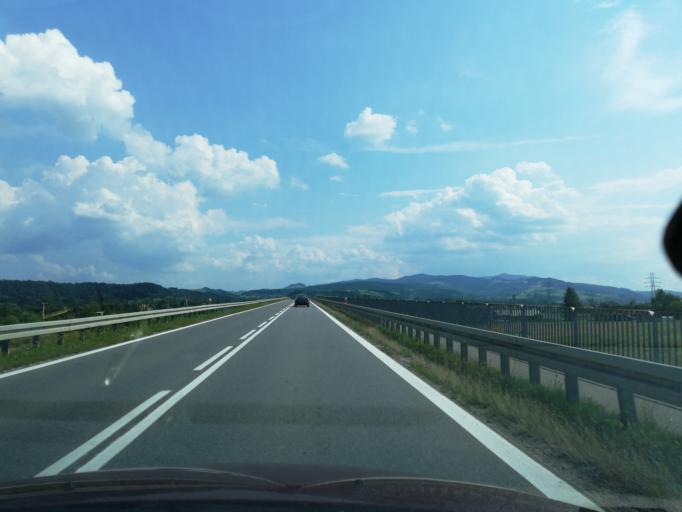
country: PL
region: Lesser Poland Voivodeship
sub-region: Powiat nowosadecki
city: Stary Sacz
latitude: 49.5747
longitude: 20.6446
